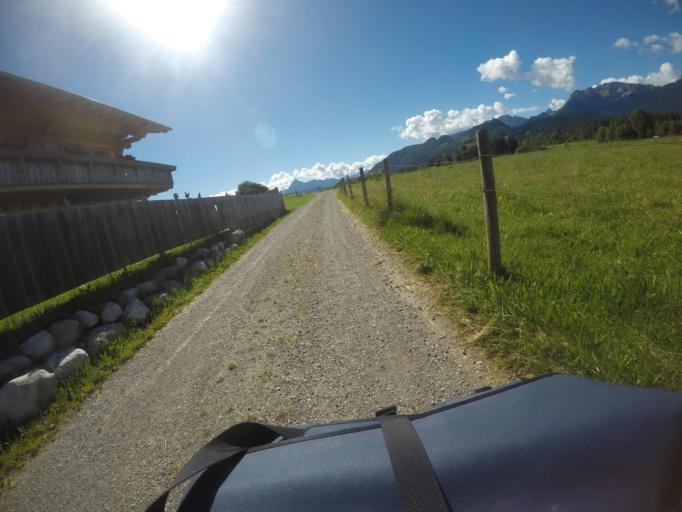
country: DE
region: Bavaria
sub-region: Swabia
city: Pfronten
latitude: 47.5954
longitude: 10.5729
